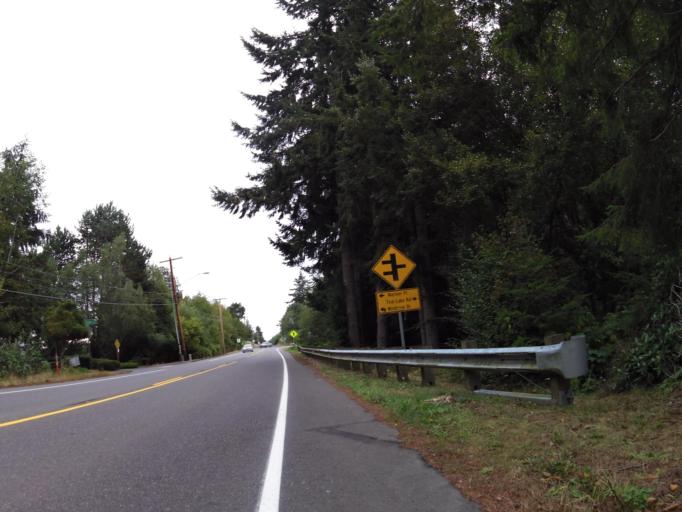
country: US
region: Washington
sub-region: Jefferson County
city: Port Ludlow
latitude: 47.9114
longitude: -122.6859
